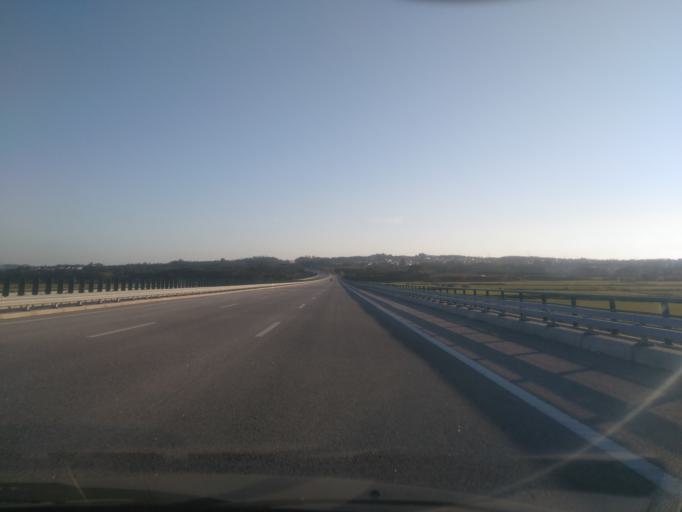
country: PT
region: Coimbra
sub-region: Figueira da Foz
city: Lavos
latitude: 40.0987
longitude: -8.7523
